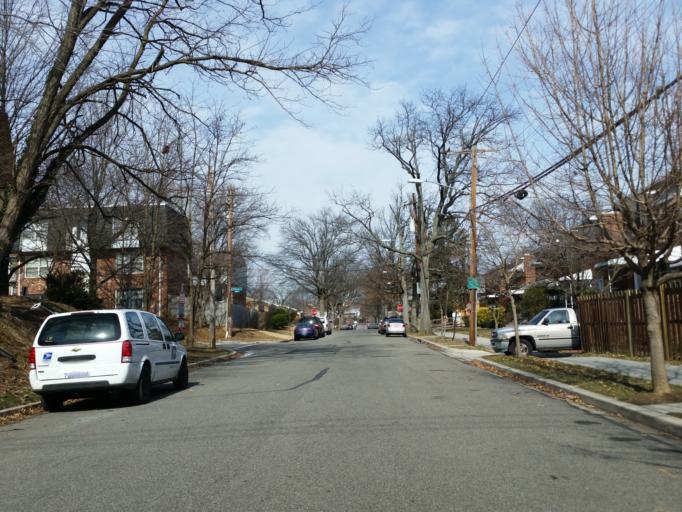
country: US
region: Maryland
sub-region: Montgomery County
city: Silver Spring
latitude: 38.9785
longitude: -77.0245
